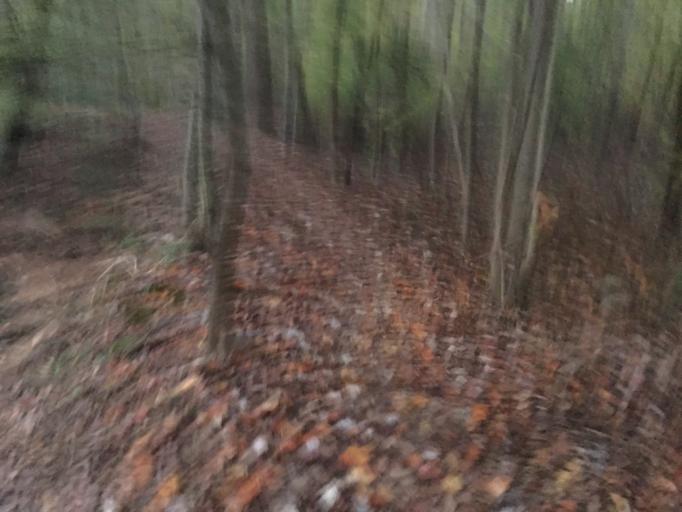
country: US
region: North Carolina
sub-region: Wake County
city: West Raleigh
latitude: 35.8705
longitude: -78.6019
